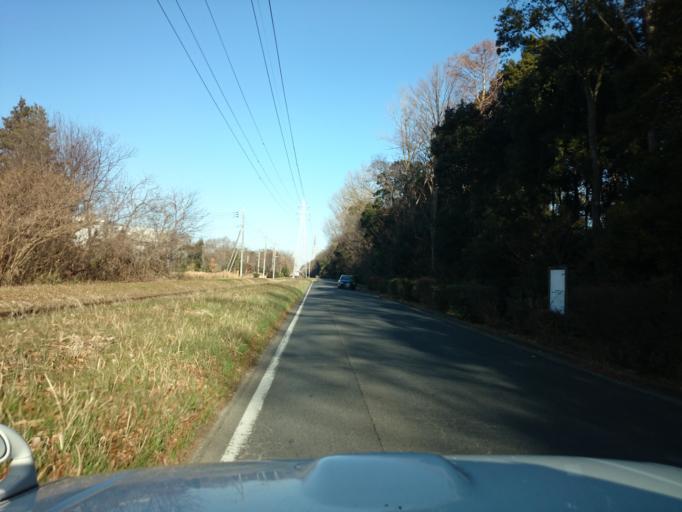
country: JP
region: Ibaraki
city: Tsukuba
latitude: 36.1157
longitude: 140.0924
